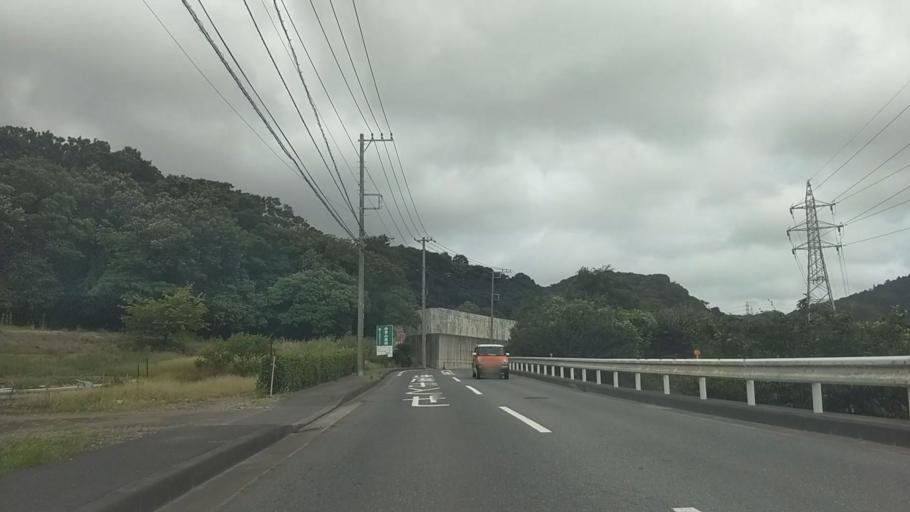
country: JP
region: Kanagawa
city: Yokosuka
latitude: 35.2318
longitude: 139.6329
